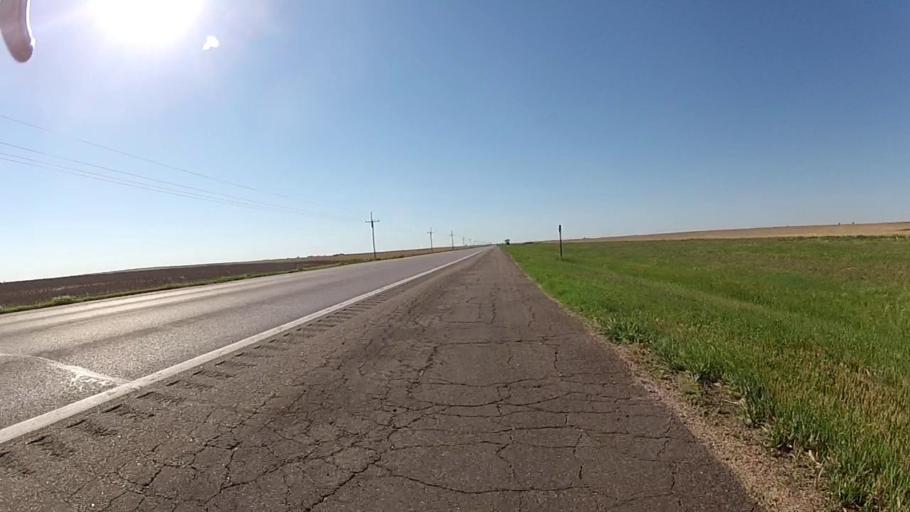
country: US
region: Kansas
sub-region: Ford County
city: Dodge City
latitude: 37.6019
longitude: -99.7029
